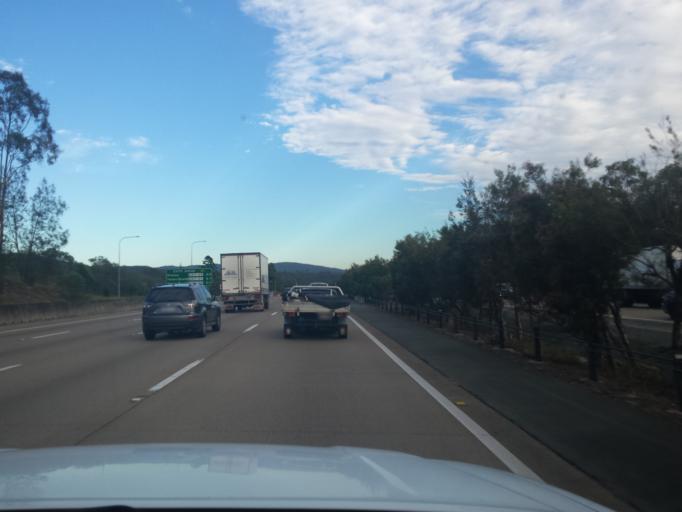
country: AU
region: Queensland
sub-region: Gold Coast
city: Ormeau Hills
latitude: -27.8204
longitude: 153.2885
